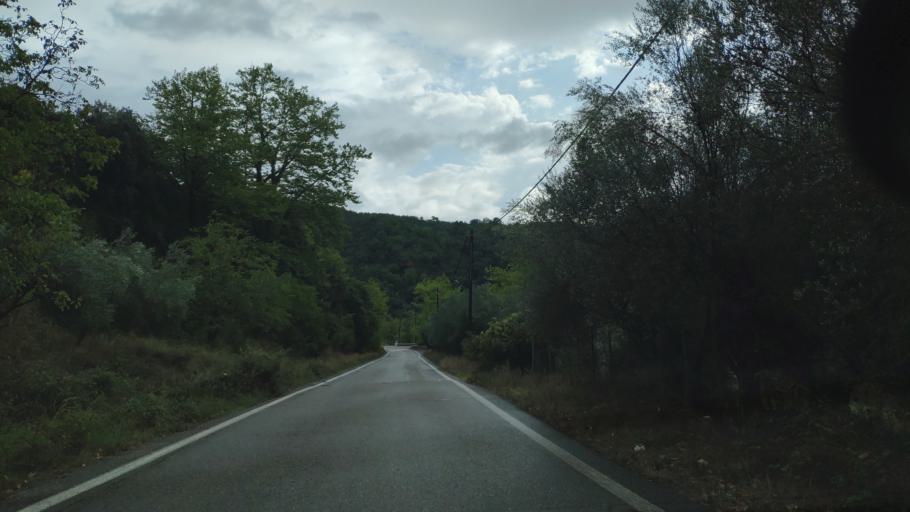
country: GR
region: West Greece
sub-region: Nomos Aitolias kai Akarnanias
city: Sardinia
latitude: 38.9260
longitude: 21.3547
